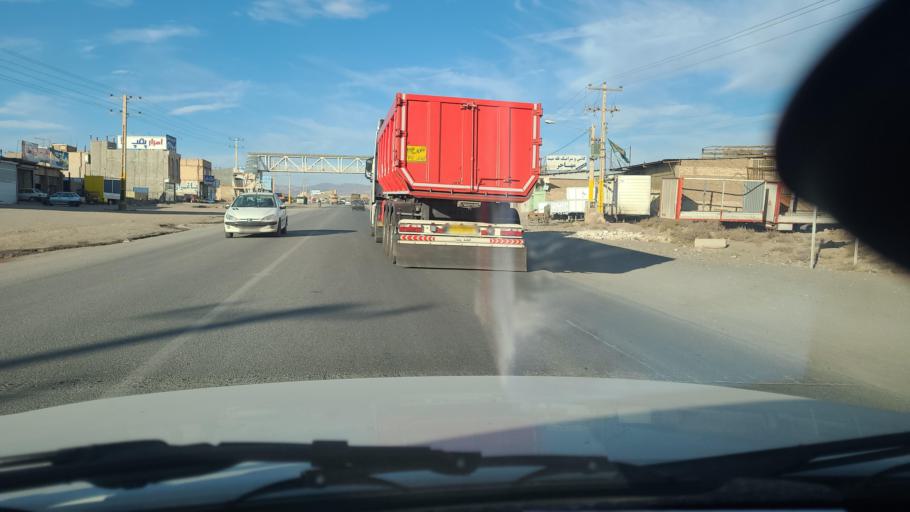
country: IR
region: Razavi Khorasan
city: Sabzevar
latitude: 36.2206
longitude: 57.6515
